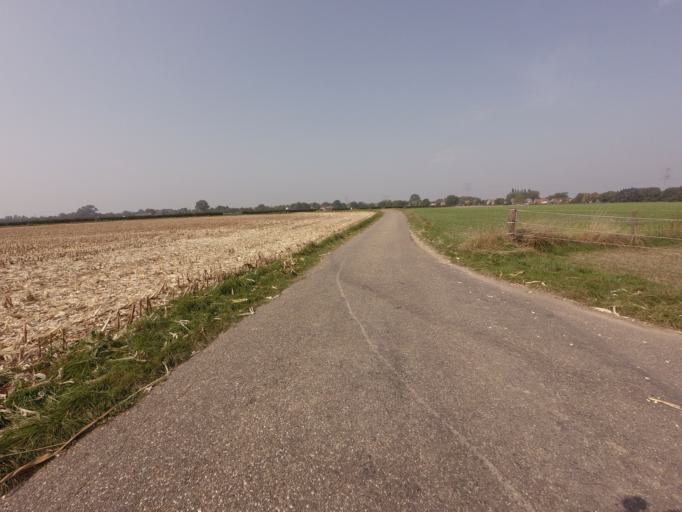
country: BE
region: Flanders
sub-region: Provincie Limburg
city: Maaseik
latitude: 51.1161
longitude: 5.8253
